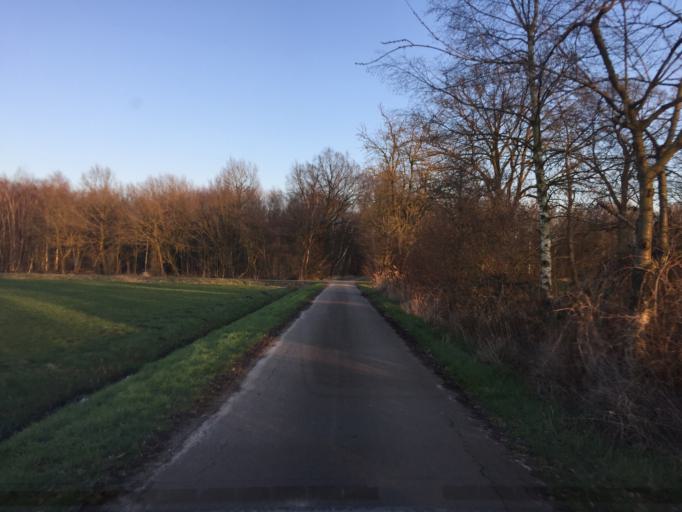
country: DE
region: Lower Saxony
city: Varrel
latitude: 52.6673
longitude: 8.7554
